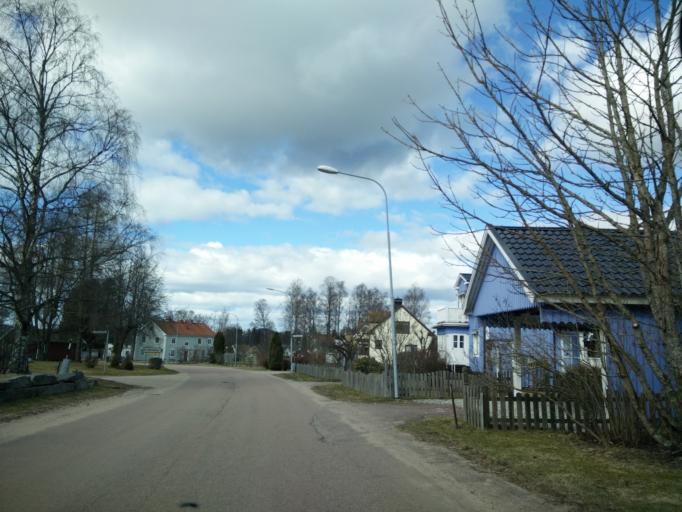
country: SE
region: Vaermland
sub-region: Hagfors Kommun
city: Hagfors
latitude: 59.9964
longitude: 13.5959
